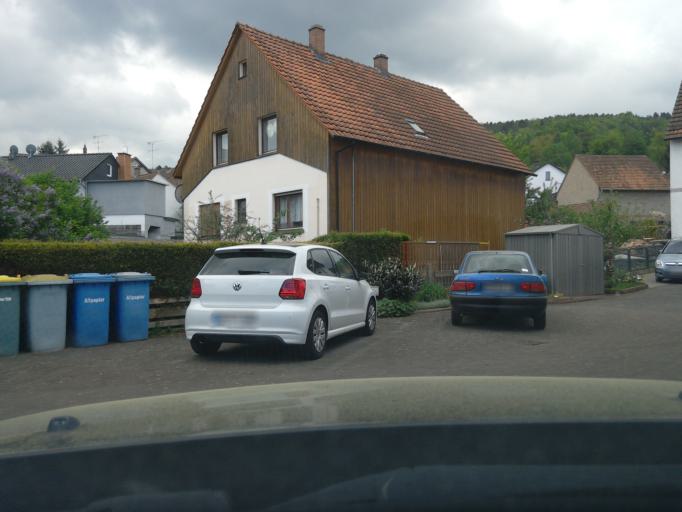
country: DE
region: Hesse
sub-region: Regierungsbezirk Darmstadt
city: Gelnhausen
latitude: 50.1792
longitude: 9.2339
